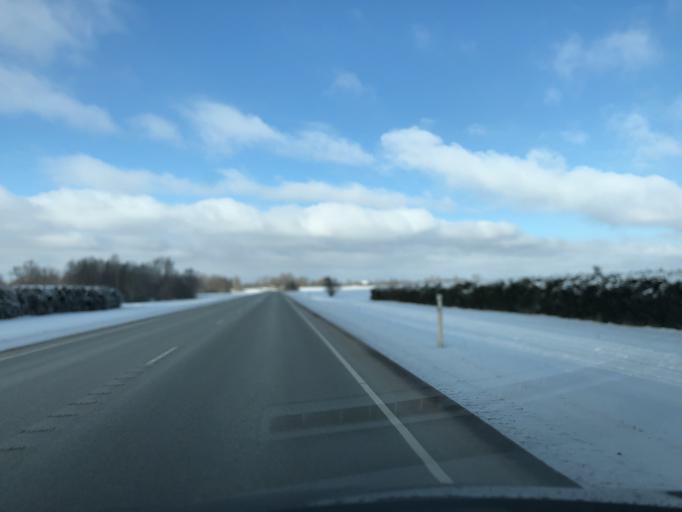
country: EE
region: Jaervamaa
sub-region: Paide linn
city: Paide
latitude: 58.8569
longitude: 25.7202
